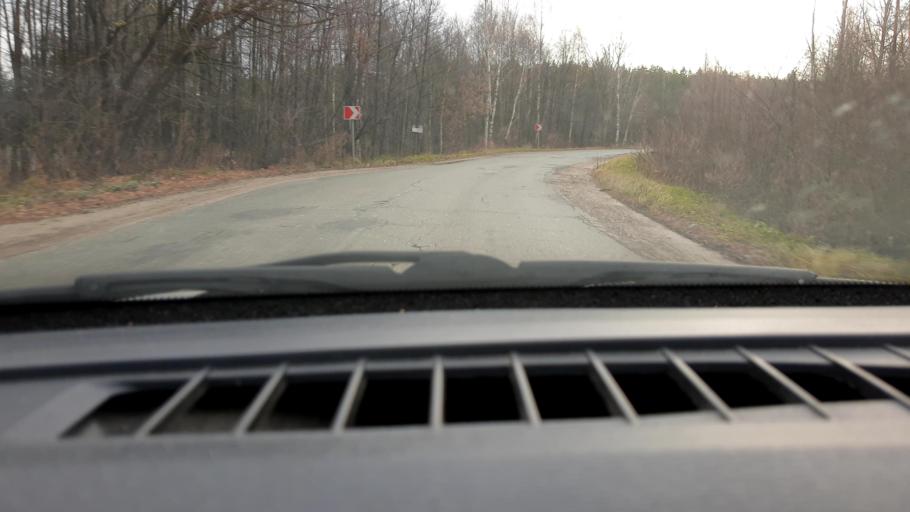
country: RU
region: Nizjnij Novgorod
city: Neklyudovo
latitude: 56.4224
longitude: 43.9260
